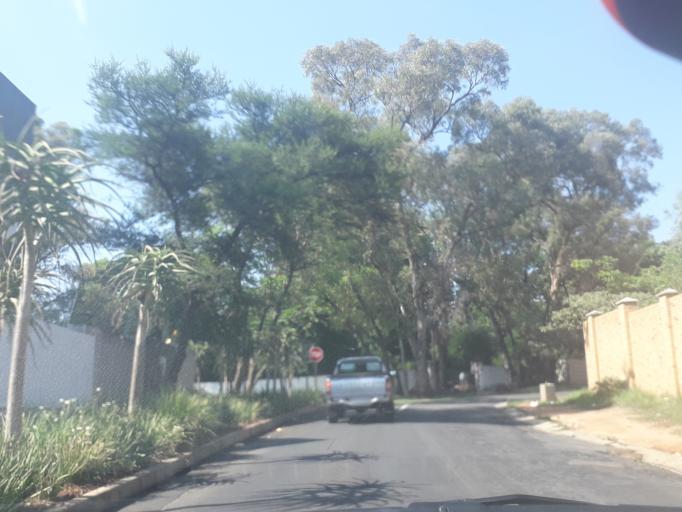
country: ZA
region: Gauteng
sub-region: City of Johannesburg Metropolitan Municipality
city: Johannesburg
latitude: -26.1073
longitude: 28.0675
